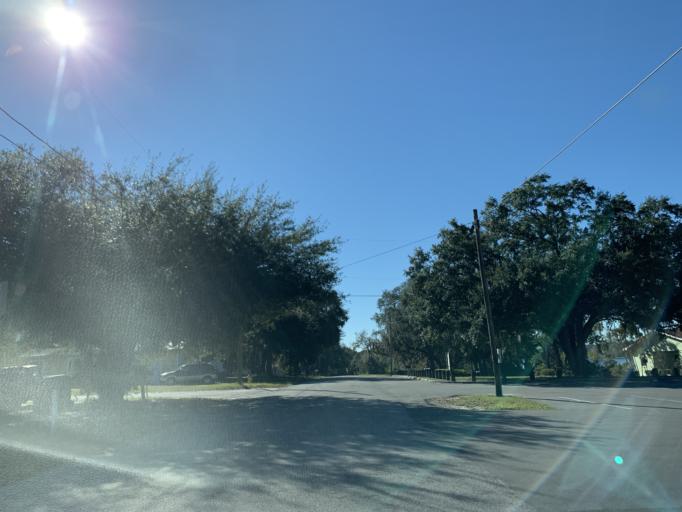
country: US
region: Florida
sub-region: Hillsborough County
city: Temple Terrace
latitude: 28.0241
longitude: -82.4182
